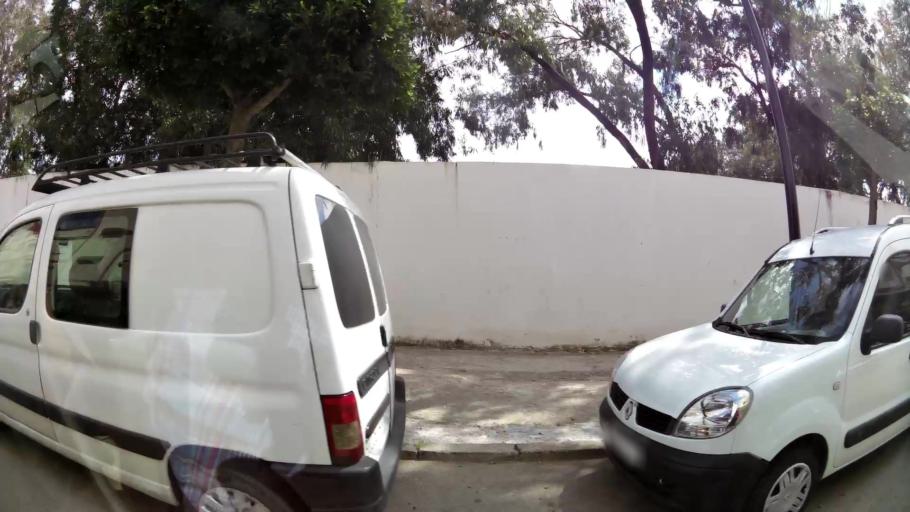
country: MA
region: Tanger-Tetouan
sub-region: Tanger-Assilah
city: Tangier
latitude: 35.7742
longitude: -5.8253
